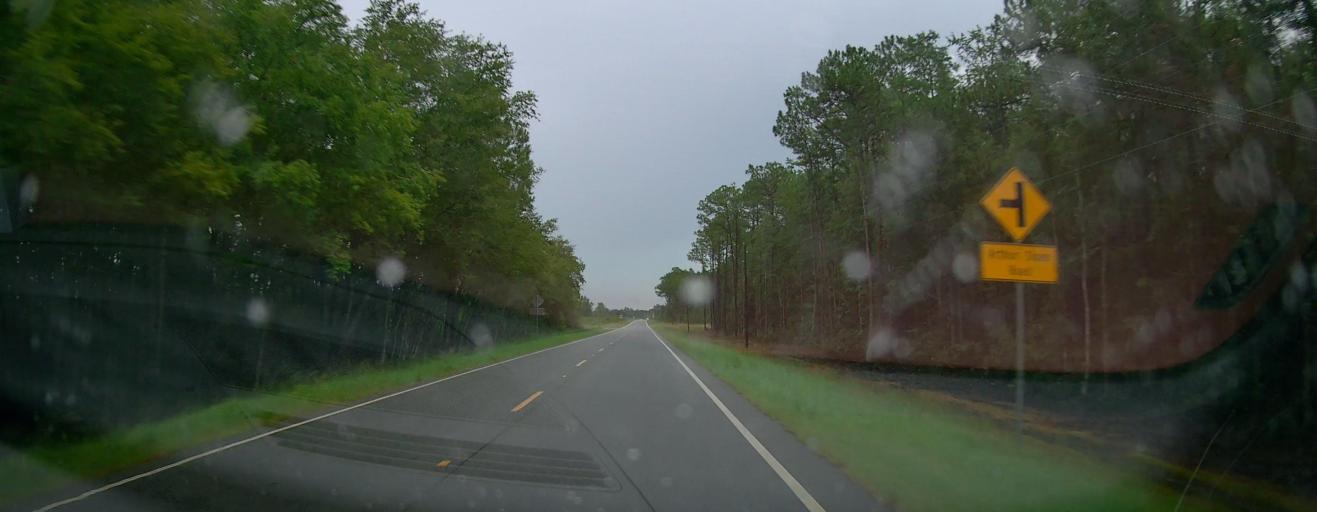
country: US
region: Georgia
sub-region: Brantley County
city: Nahunta
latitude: 31.3336
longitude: -81.9420
